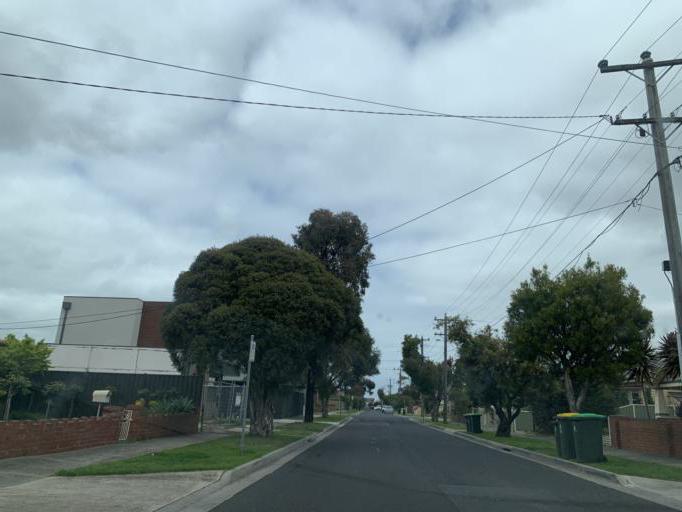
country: AU
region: Victoria
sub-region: Moreland
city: Pascoe Vale South
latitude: -37.7356
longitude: 144.9411
